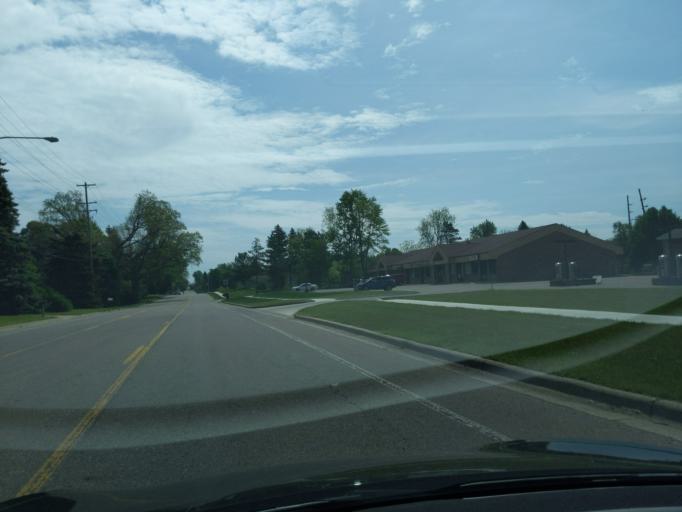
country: US
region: Michigan
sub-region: Ingham County
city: Holt
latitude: 42.6547
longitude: -84.5275
